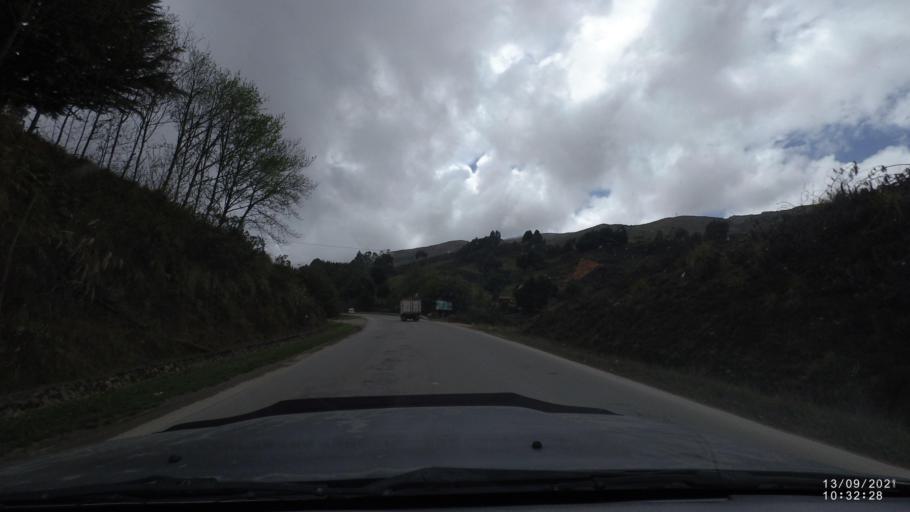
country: BO
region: Cochabamba
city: Colomi
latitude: -17.2485
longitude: -65.8918
